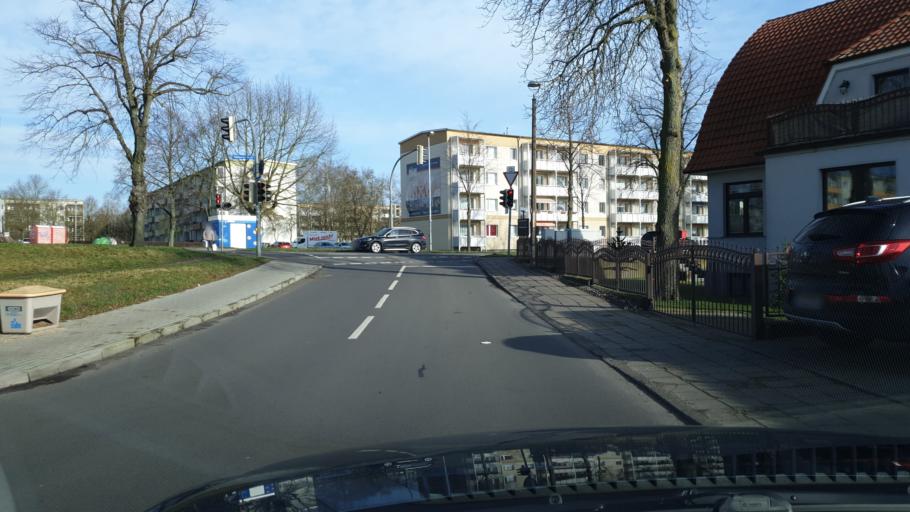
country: DE
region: Mecklenburg-Vorpommern
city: Lankow
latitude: 53.6472
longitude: 11.3570
